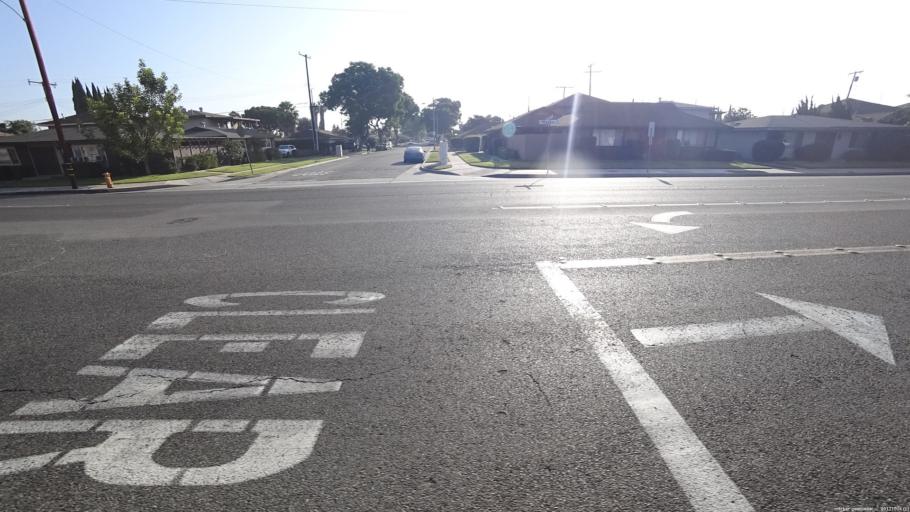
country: US
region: California
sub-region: Orange County
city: Garden Grove
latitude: 33.7771
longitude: -117.9062
